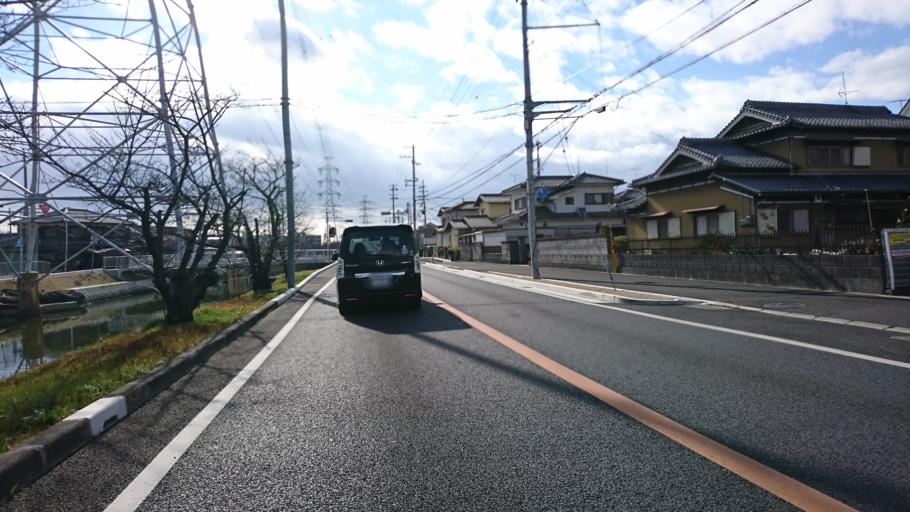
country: JP
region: Hyogo
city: Kakogawacho-honmachi
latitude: 34.7768
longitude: 134.7789
